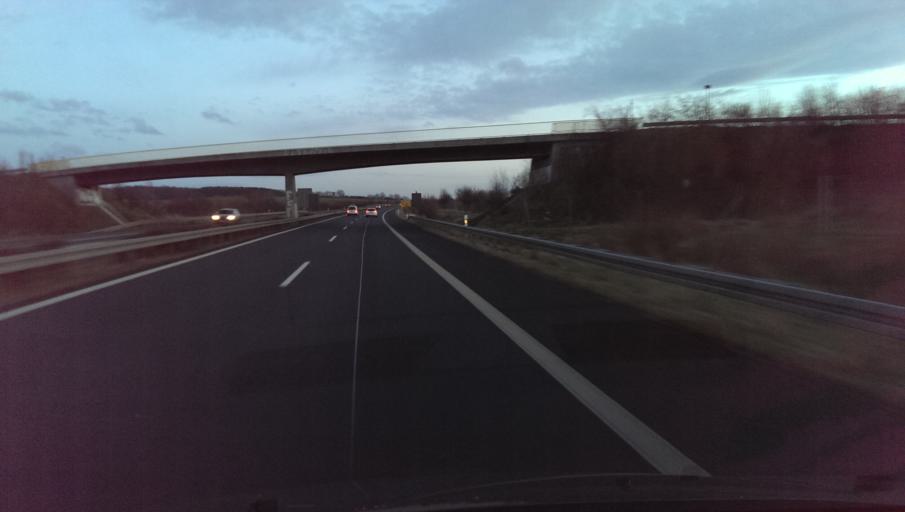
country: DE
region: Saxony-Anhalt
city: Stapelburg
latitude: 51.9306
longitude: 10.6461
